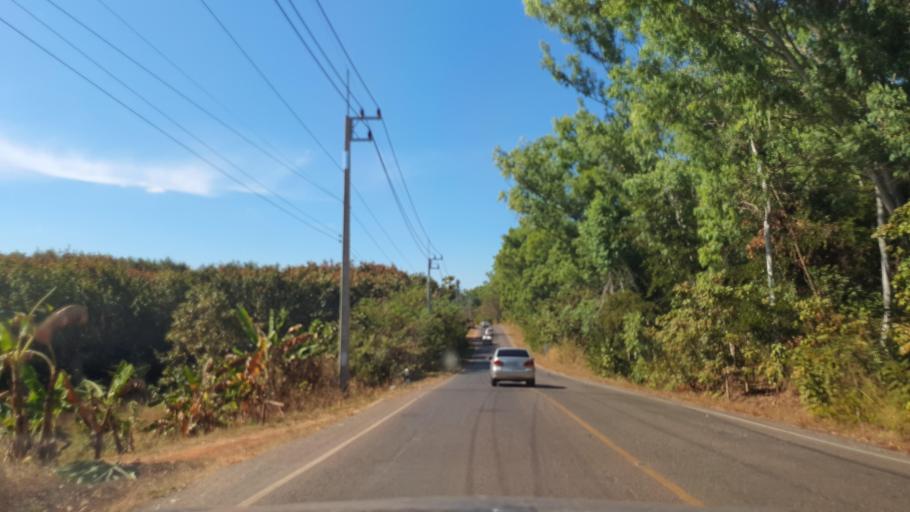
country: TH
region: Kalasin
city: Khao Wong
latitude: 16.7620
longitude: 104.1495
